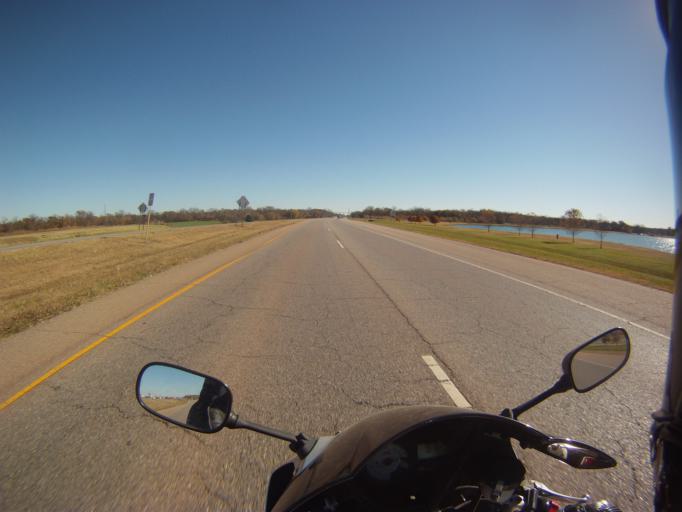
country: US
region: Oklahoma
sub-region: Payne County
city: Stillwater
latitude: 36.1159
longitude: -97.1097
